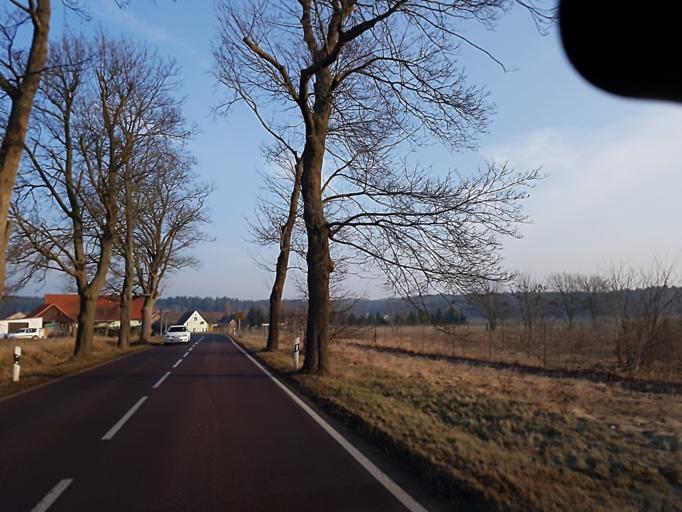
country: DE
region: Saxony-Anhalt
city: Coswig
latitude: 51.9925
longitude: 12.4718
